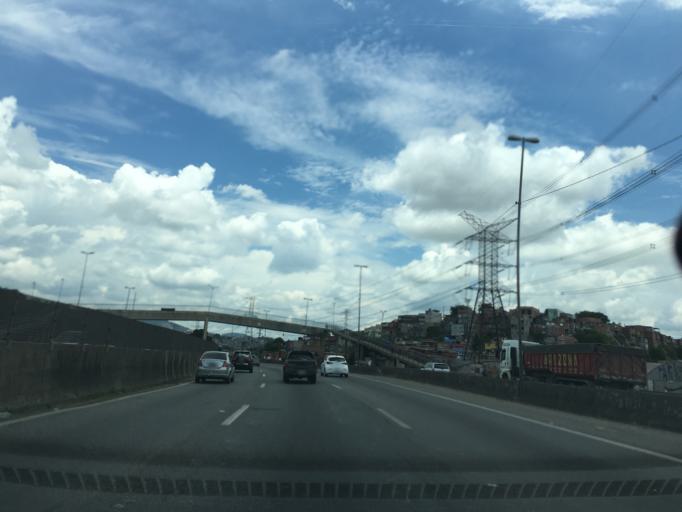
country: BR
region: Sao Paulo
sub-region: Guarulhos
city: Guarulhos
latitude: -23.4756
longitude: -46.5605
